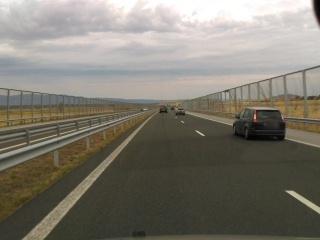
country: BG
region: Yambol
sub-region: Obshtina Yambol
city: Yambol
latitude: 42.5271
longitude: 26.3908
